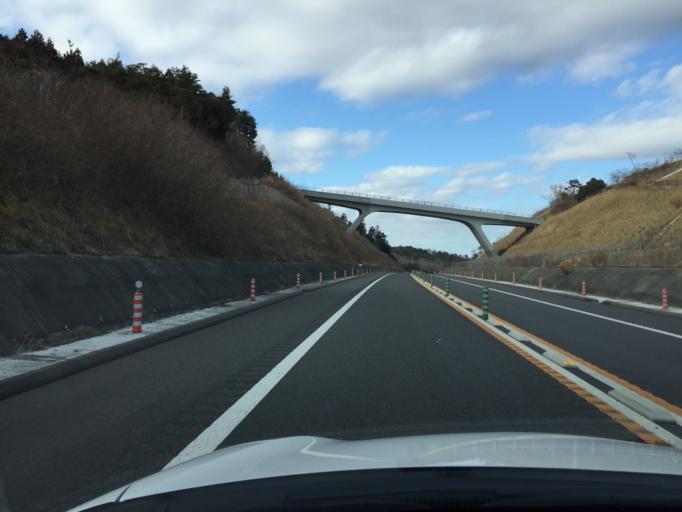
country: JP
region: Fukushima
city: Namie
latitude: 37.4400
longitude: 140.9580
